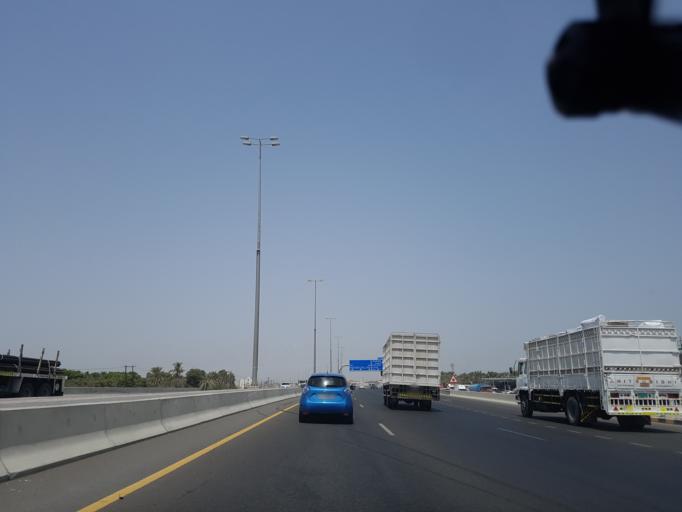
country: OM
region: Al Batinah
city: Al Sohar
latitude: 24.4156
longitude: 56.6298
